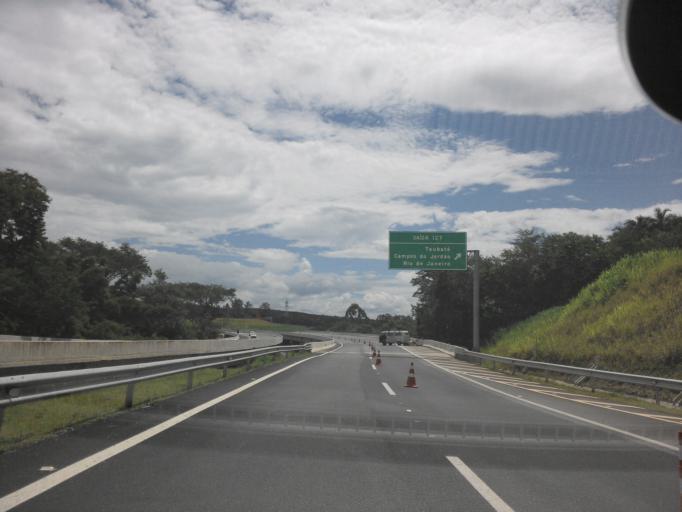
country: BR
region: Sao Paulo
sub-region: Taubate
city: Taubate
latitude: -23.0969
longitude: -45.6086
